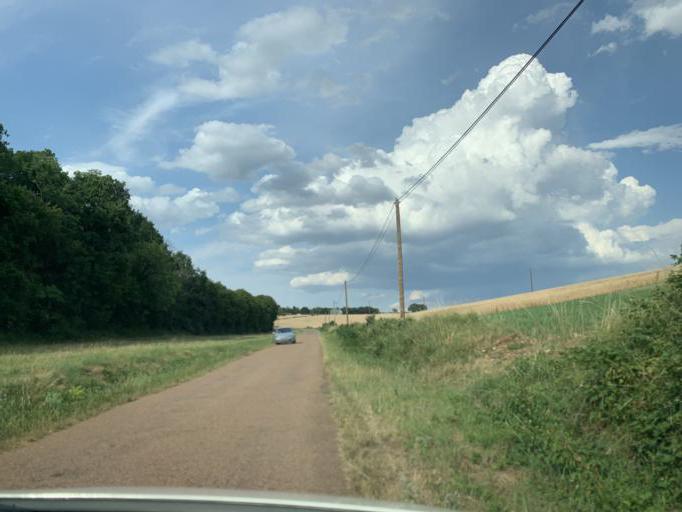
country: FR
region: Bourgogne
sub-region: Departement de l'Yonne
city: Fontenailles
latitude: 47.4921
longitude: 3.4240
